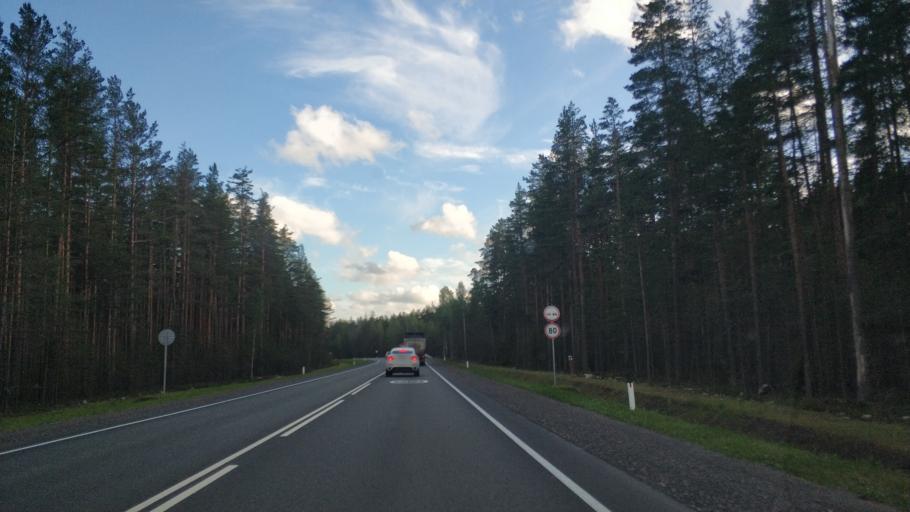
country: RU
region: Leningrad
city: Priozersk
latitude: 60.8827
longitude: 30.1607
